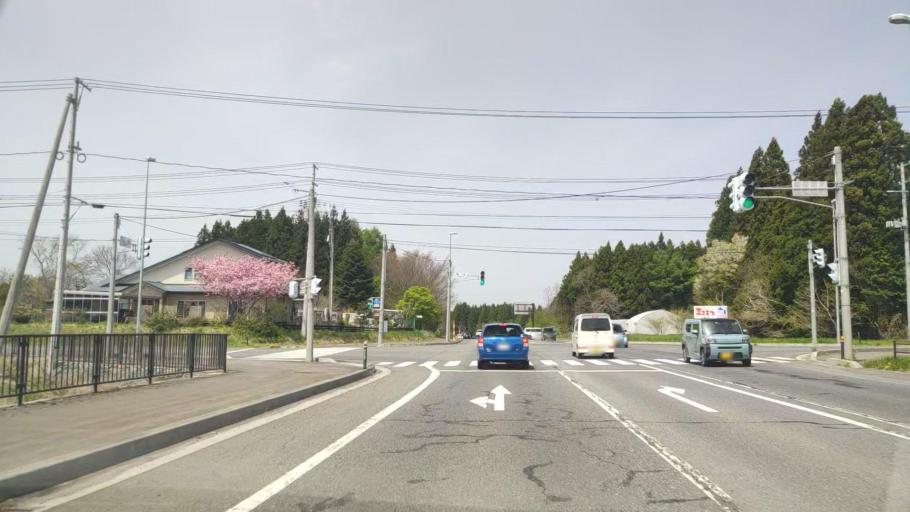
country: JP
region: Aomori
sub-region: Misawa Shi
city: Inuotose
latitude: 40.7079
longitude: 141.1611
